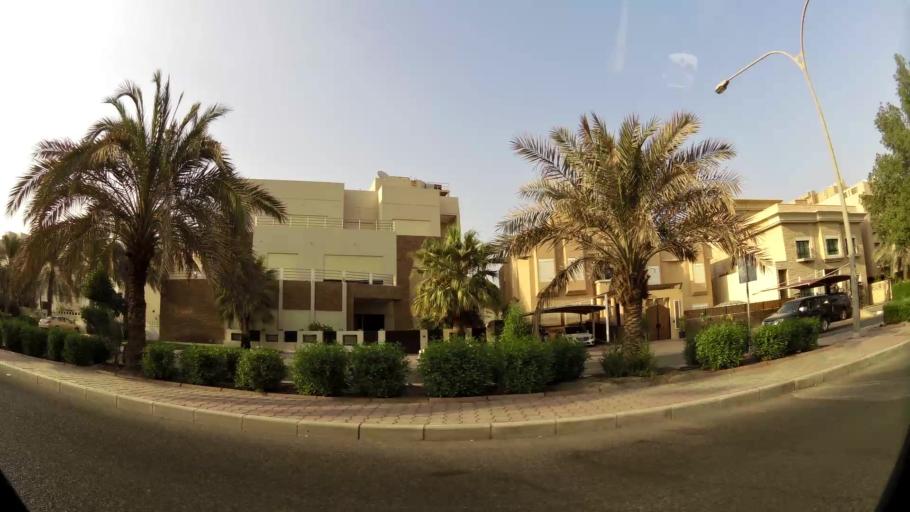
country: KW
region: Muhafazat Hawalli
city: Hawalli
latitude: 29.3131
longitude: 48.0238
